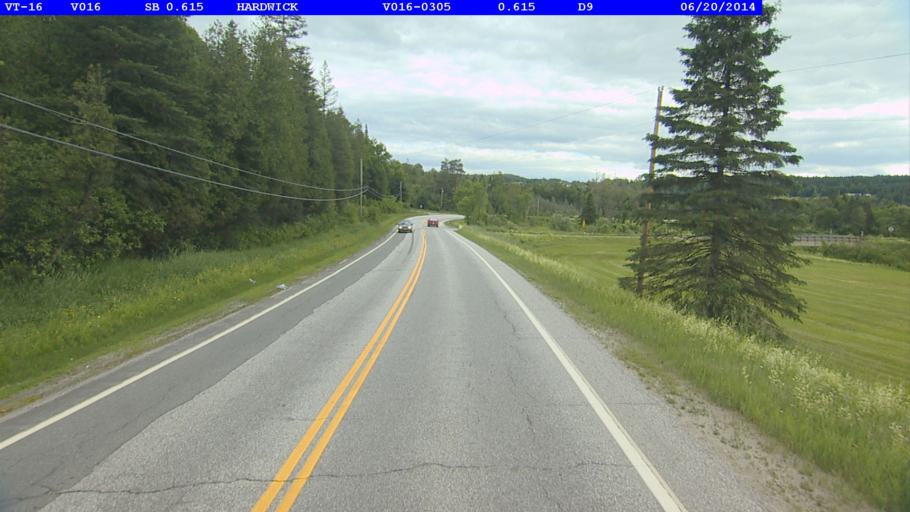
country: US
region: Vermont
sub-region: Caledonia County
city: Hardwick
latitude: 44.5065
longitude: -72.3177
